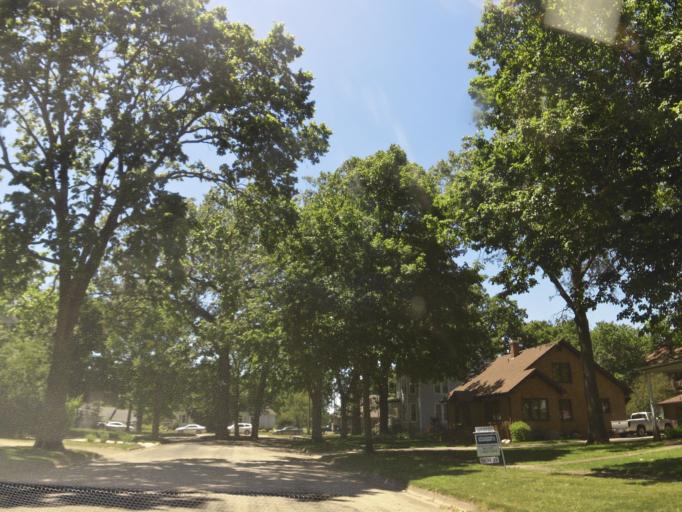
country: US
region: Illinois
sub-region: Livingston County
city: Forrest
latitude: 40.7513
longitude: -88.4135
